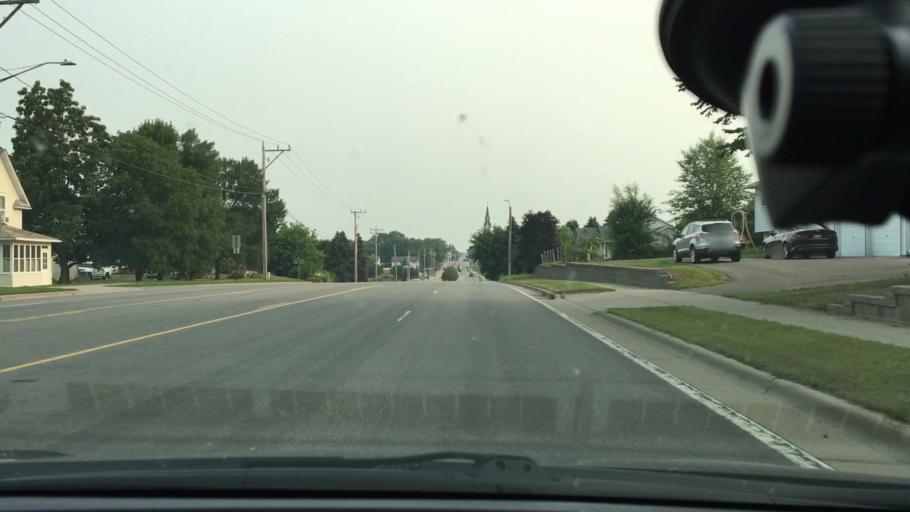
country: US
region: Minnesota
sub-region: Wright County
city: Saint Michael
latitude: 45.2174
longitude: -93.6648
